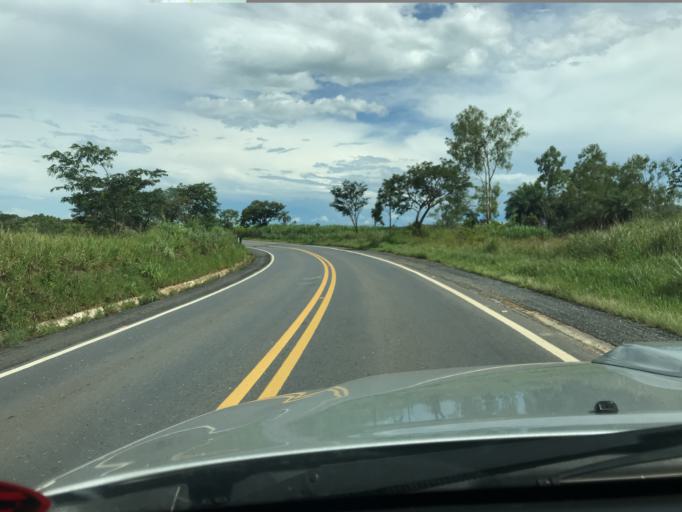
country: BR
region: Minas Gerais
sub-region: Campos Altos
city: Campos Altos
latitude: -19.8101
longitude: -46.0330
